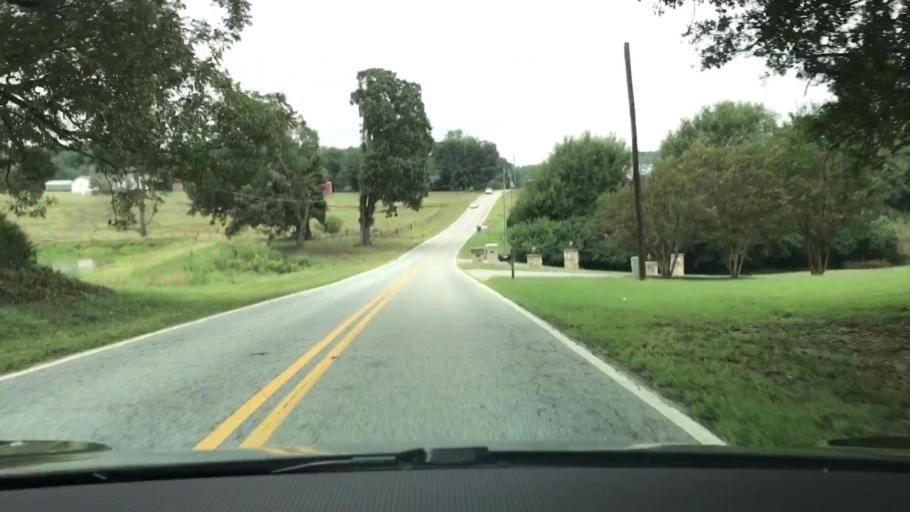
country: US
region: Georgia
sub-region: Barrow County
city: Auburn
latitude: 34.0436
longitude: -83.8086
